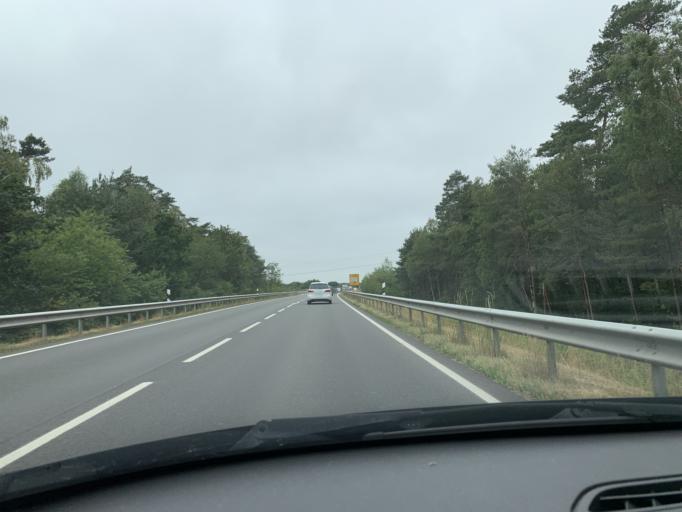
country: DE
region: Lower Saxony
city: Lingen
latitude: 52.4922
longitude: 7.3058
